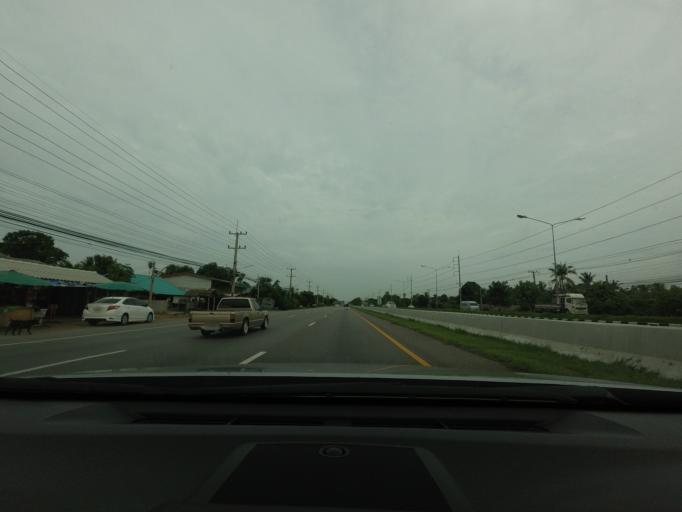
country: TH
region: Phetchaburi
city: Khao Yoi
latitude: 13.1607
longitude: 99.8452
